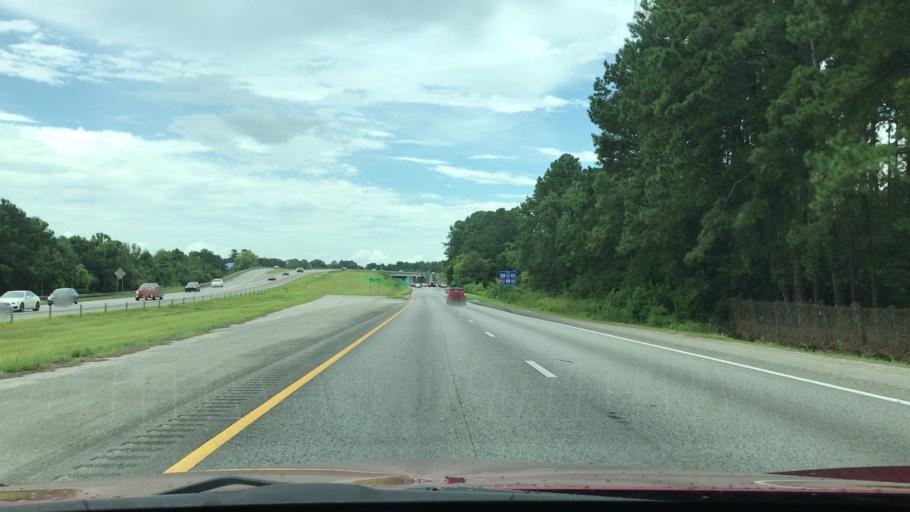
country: US
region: South Carolina
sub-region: Charleston County
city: Shell Point
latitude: 32.7954
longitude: -80.0344
